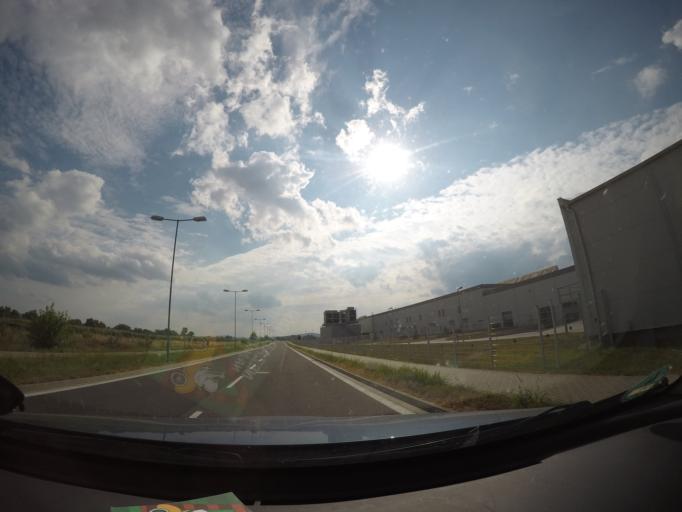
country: SK
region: Trenciansky
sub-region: Okres Trencin
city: Trencin
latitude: 48.8844
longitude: 17.9959
